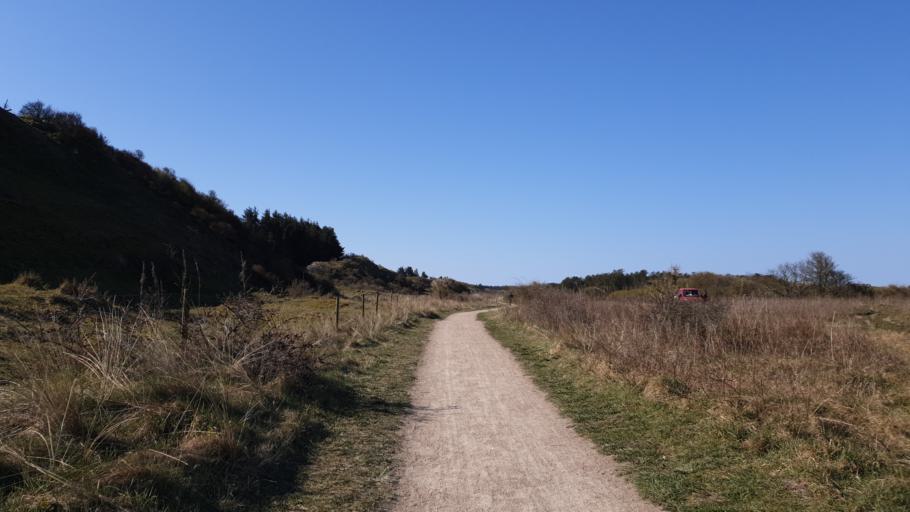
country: DK
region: North Denmark
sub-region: Hjorring Kommune
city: Hjorring
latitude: 57.4948
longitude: 9.8476
